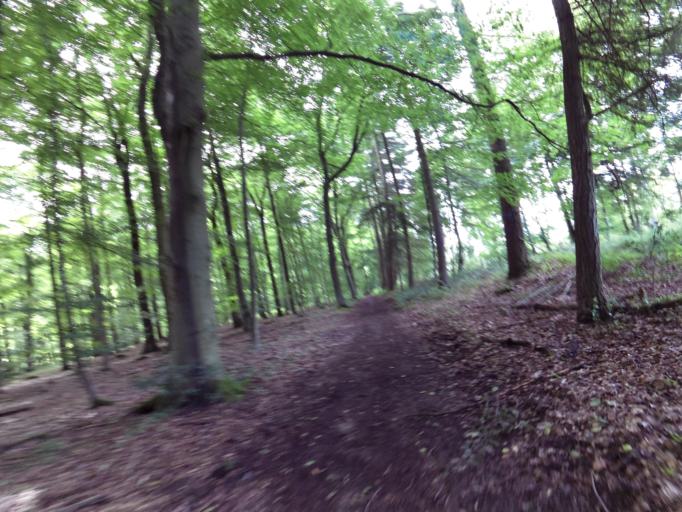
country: DE
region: Rheinland-Pfalz
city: Dernau
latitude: 50.5671
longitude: 7.0642
